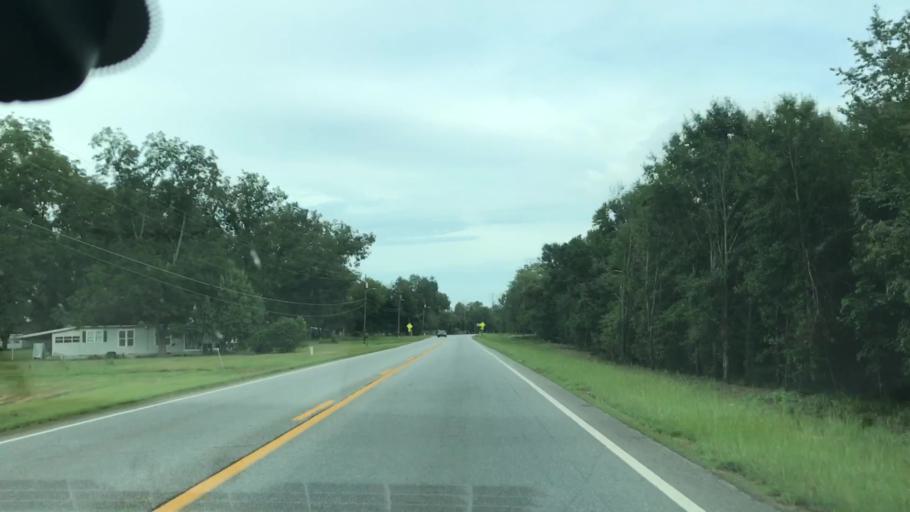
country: US
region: Georgia
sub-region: Quitman County
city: Georgetown
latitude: 31.8816
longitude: -85.0888
